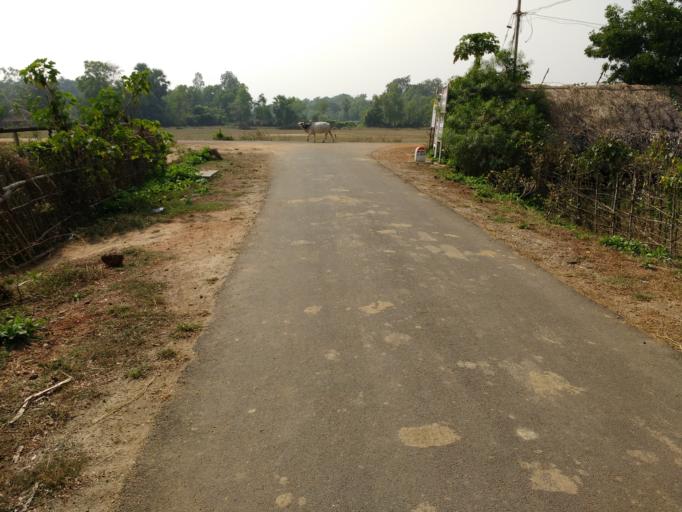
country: IN
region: Odisha
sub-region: Baleshwar
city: Soro
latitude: 21.3040
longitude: 86.7494
